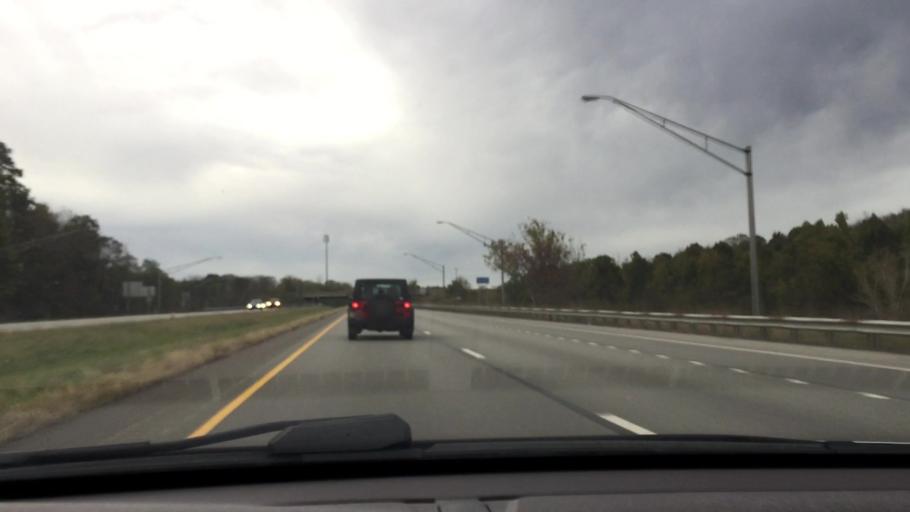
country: US
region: Pennsylvania
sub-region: Beaver County
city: New Brighton
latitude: 40.7049
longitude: -80.3693
